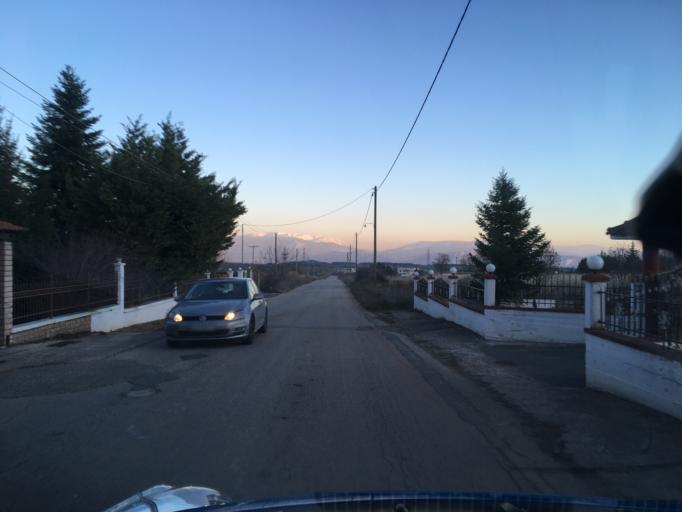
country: GR
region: West Macedonia
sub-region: Nomos Kozanis
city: Kozani
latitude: 40.2584
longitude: 21.7535
